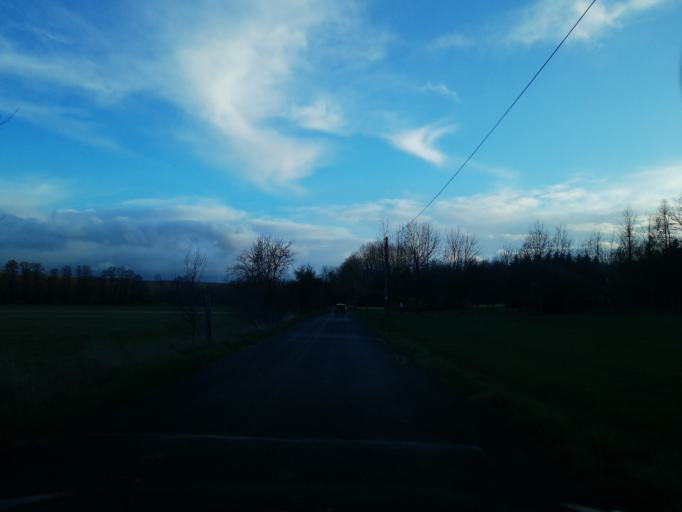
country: DE
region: Brandenburg
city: Calau
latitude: 51.7343
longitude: 13.9600
